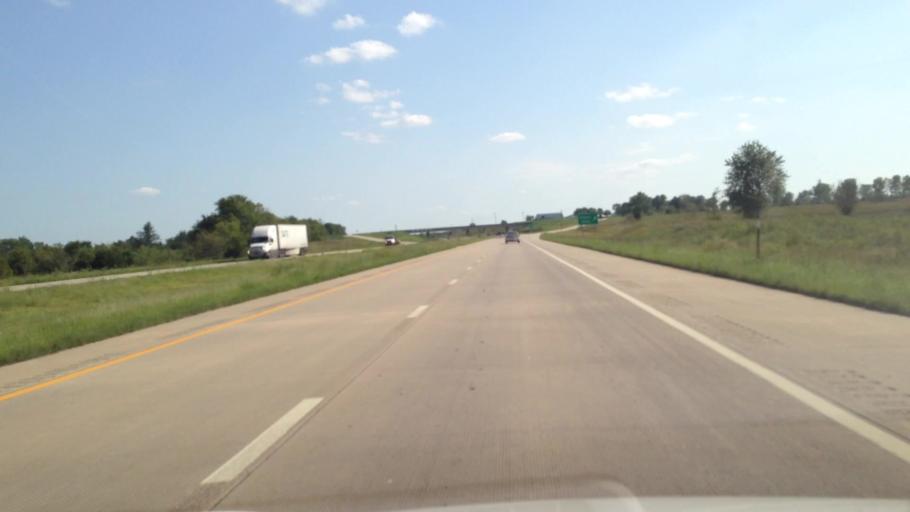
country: US
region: Kansas
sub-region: Bourbon County
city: Fort Scott
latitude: 37.8981
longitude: -94.7046
